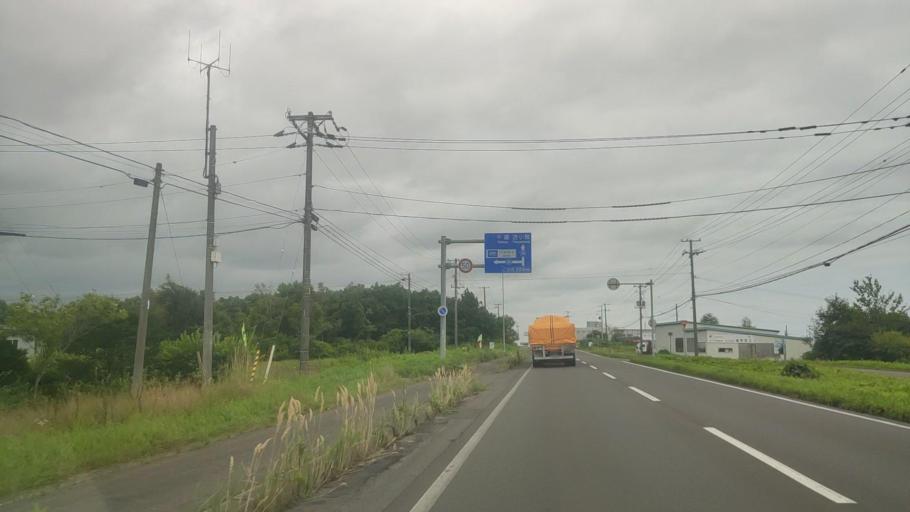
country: JP
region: Hokkaido
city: Shiraoi
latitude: 42.5250
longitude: 141.3163
